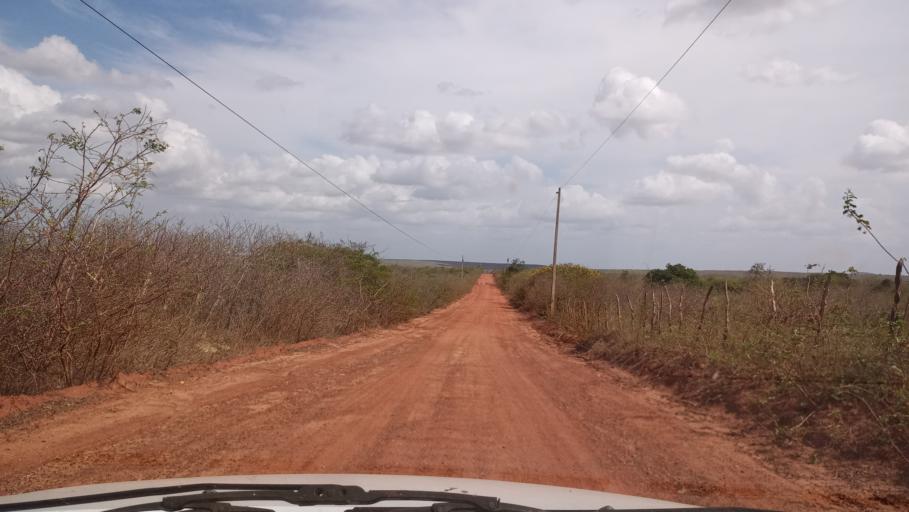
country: BR
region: Rio Grande do Norte
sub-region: Joao Camara
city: Joao Camara
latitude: -5.4564
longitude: -35.8386
